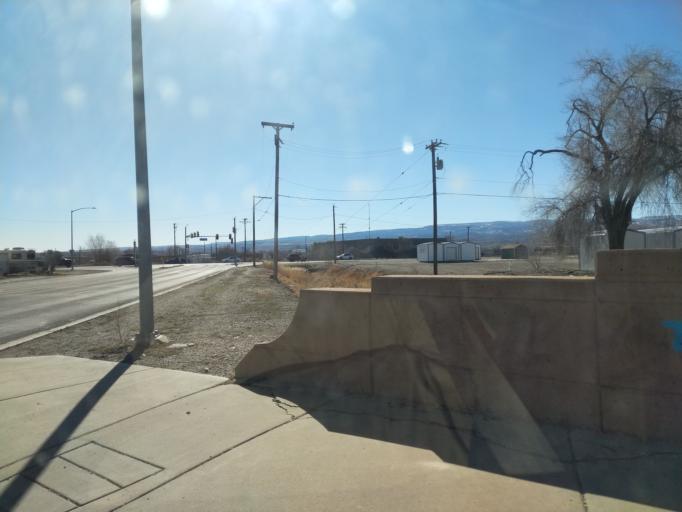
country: US
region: Colorado
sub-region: Mesa County
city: Grand Junction
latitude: 39.0701
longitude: -108.5338
